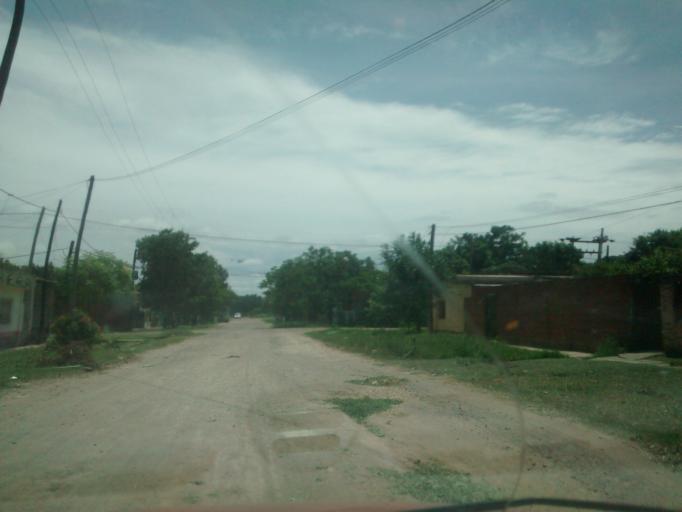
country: AR
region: Chaco
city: Resistencia
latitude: -27.4366
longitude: -58.9766
